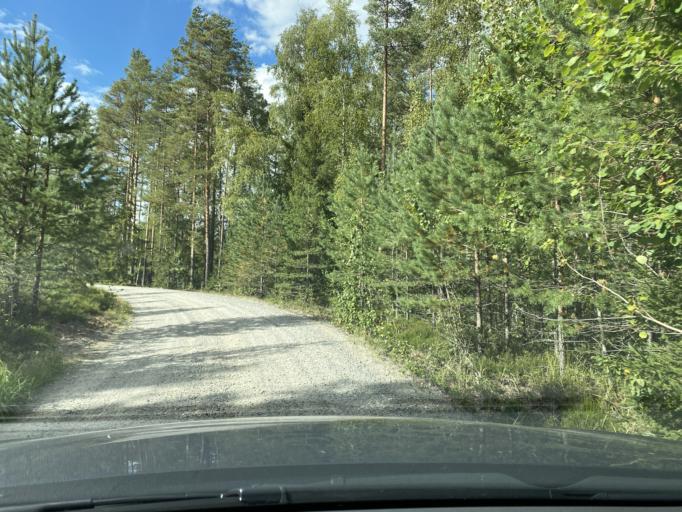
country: FI
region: Pirkanmaa
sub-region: Lounais-Pirkanmaa
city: Punkalaidun
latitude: 61.0860
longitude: 23.2605
